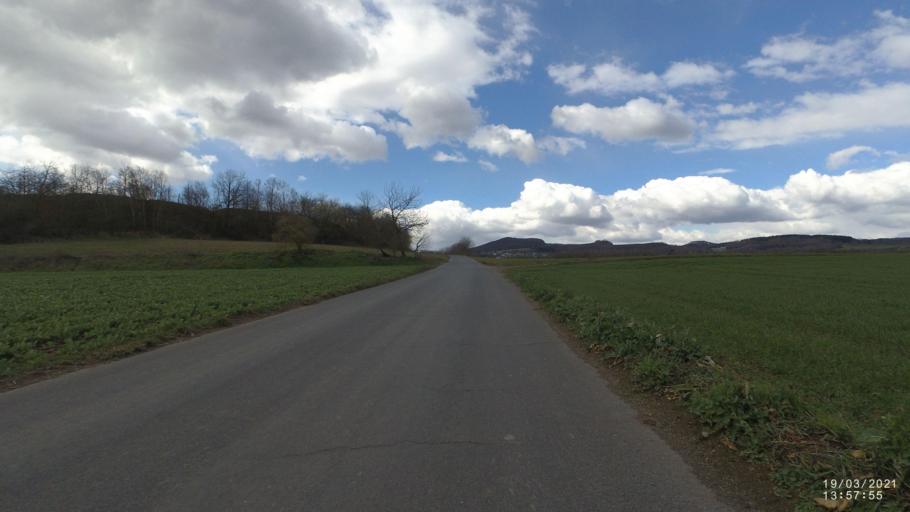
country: DE
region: Rheinland-Pfalz
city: Nickenich
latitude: 50.4048
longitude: 7.3455
